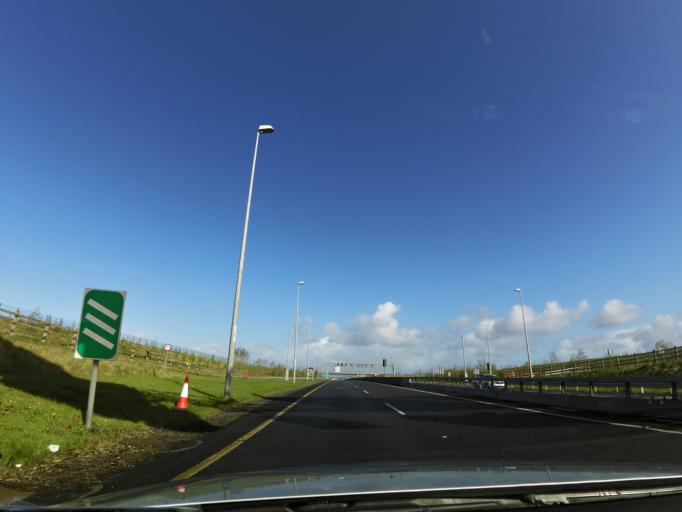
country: IE
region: Munster
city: Moyross
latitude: 52.6573
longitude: -8.6900
